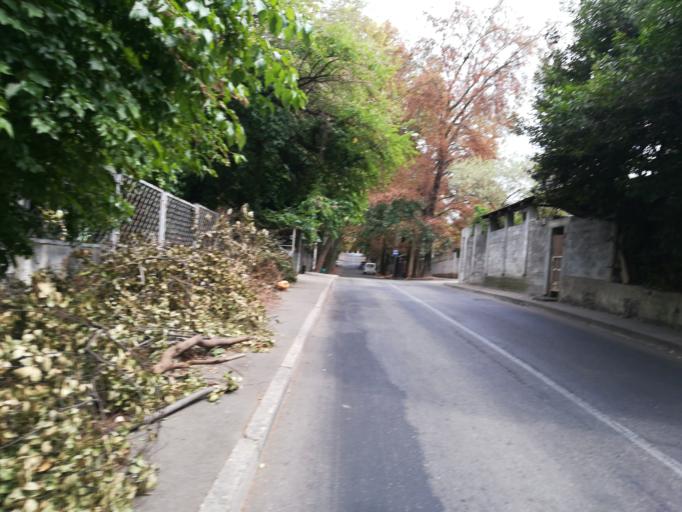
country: RU
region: Krasnodarskiy
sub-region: Sochi City
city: Sochi
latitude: 43.5909
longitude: 39.7376
